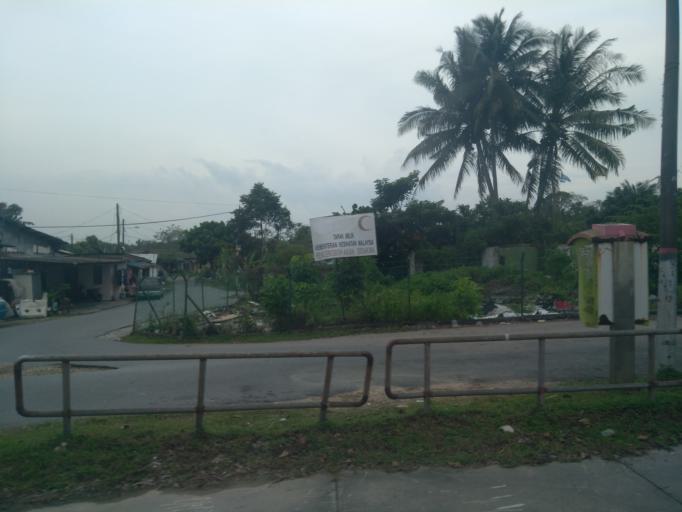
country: MY
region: Johor
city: Johor Bahru
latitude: 1.4922
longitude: 103.7076
